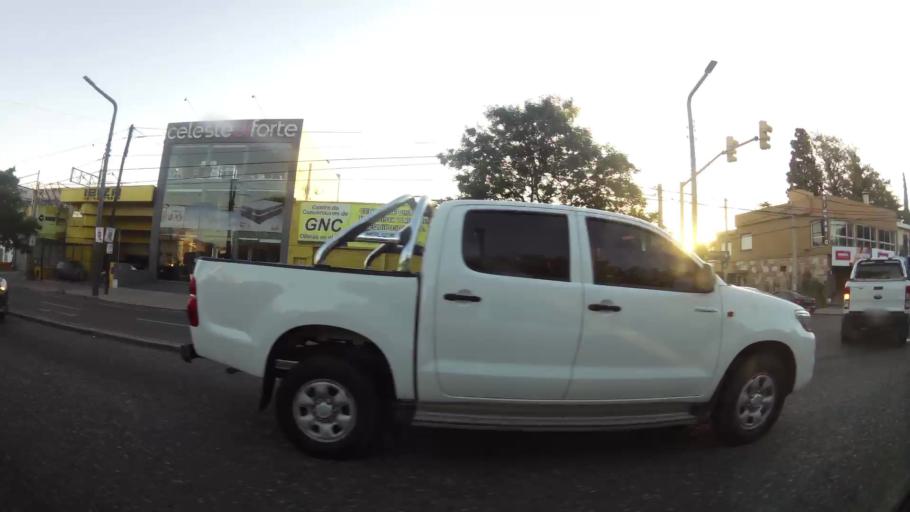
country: AR
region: Cordoba
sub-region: Departamento de Capital
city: Cordoba
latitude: -31.3840
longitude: -64.2214
